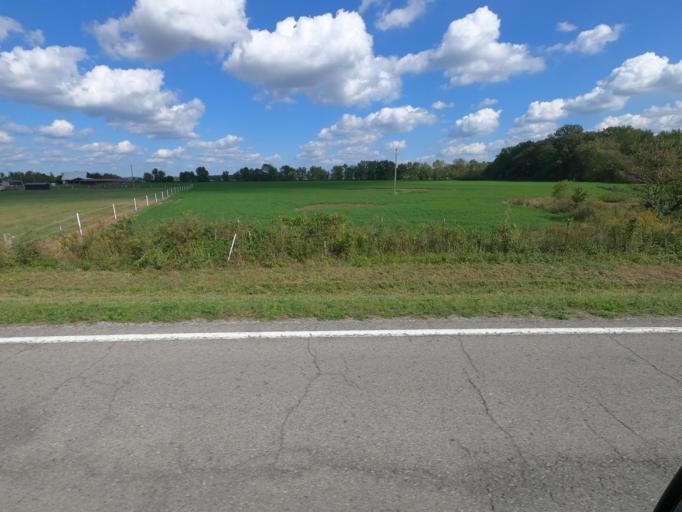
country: US
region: Illinois
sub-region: Massac County
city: Metropolis
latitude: 37.2950
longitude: -88.7564
